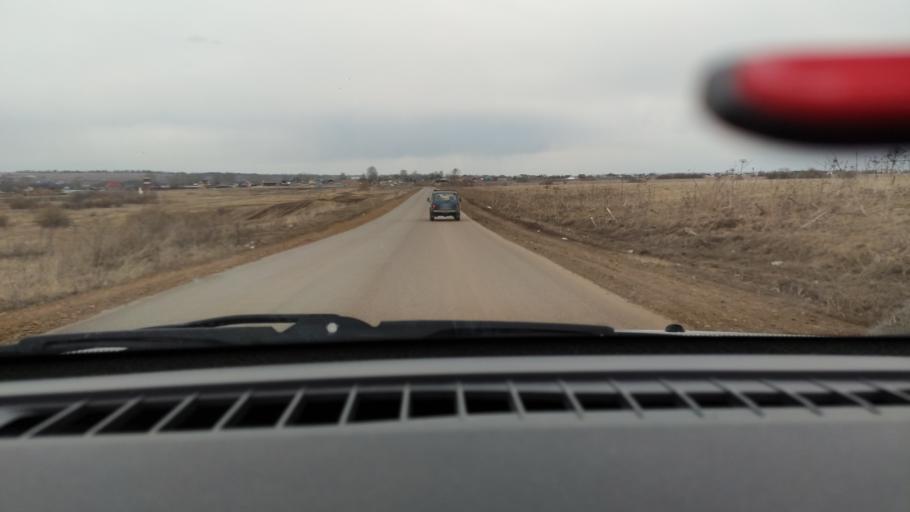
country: RU
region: Perm
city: Kultayevo
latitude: 57.9015
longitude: 55.9929
